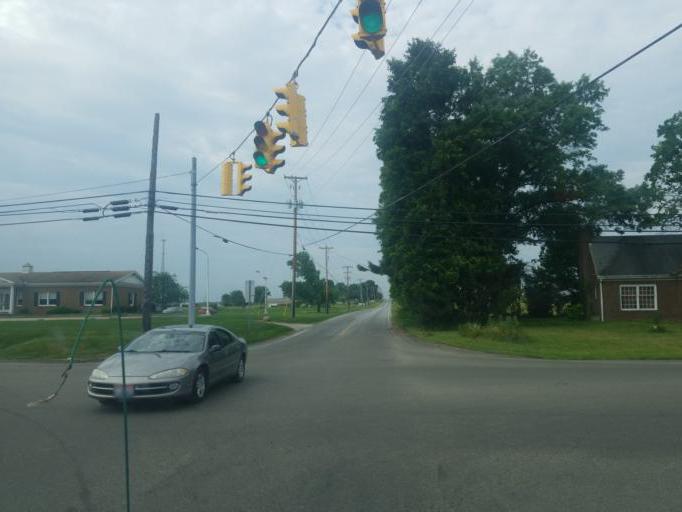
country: US
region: Ohio
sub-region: Wayne County
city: Apple Creek
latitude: 40.7977
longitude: -81.8442
